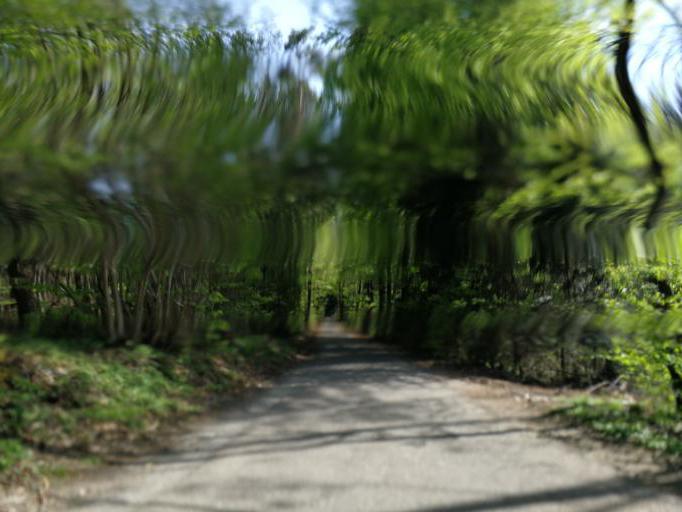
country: CH
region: Zurich
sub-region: Bezirk Hinwil
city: Hinwil
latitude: 47.3022
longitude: 8.8181
